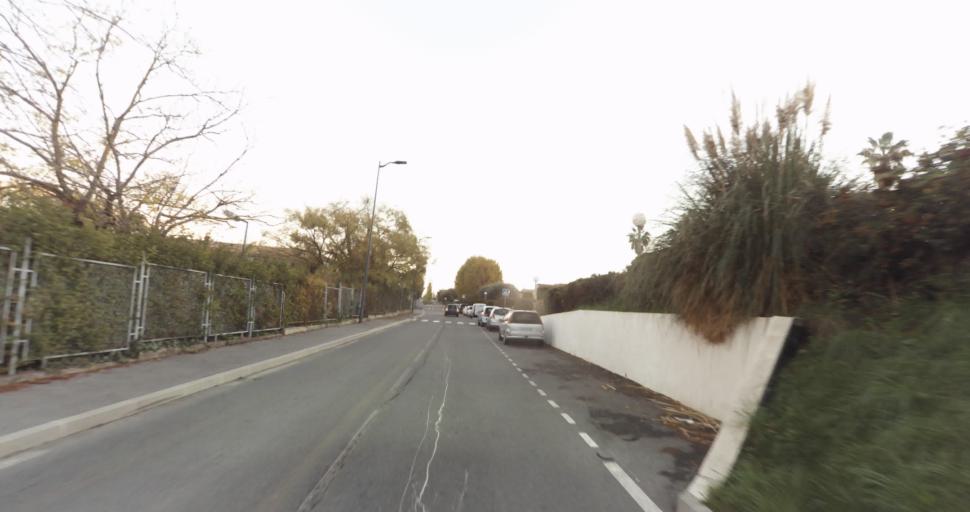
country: FR
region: Provence-Alpes-Cote d'Azur
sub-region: Departement des Alpes-Maritimes
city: Vence
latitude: 43.7199
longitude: 7.1280
